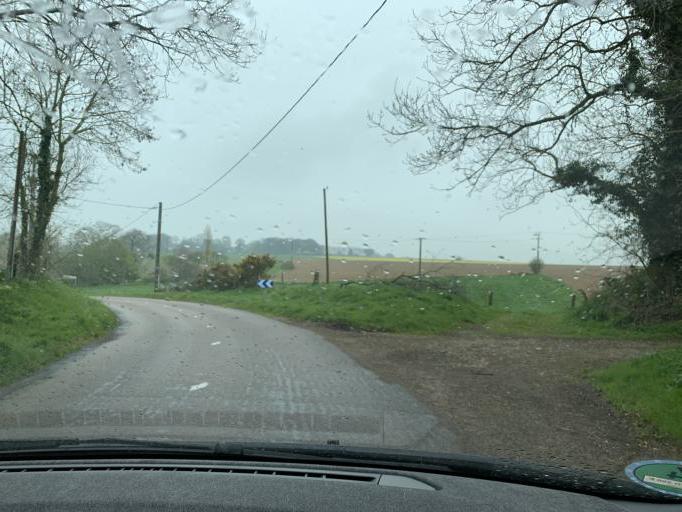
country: FR
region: Haute-Normandie
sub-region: Departement de la Seine-Maritime
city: Les Loges
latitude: 49.7182
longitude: 0.2719
